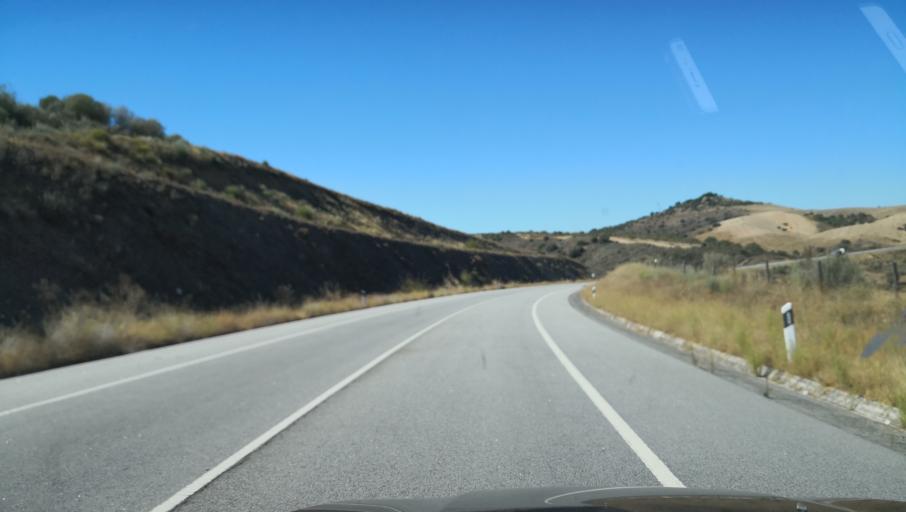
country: PT
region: Braganca
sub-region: Mirandela
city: Mirandela
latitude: 41.5200
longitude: -7.2383
